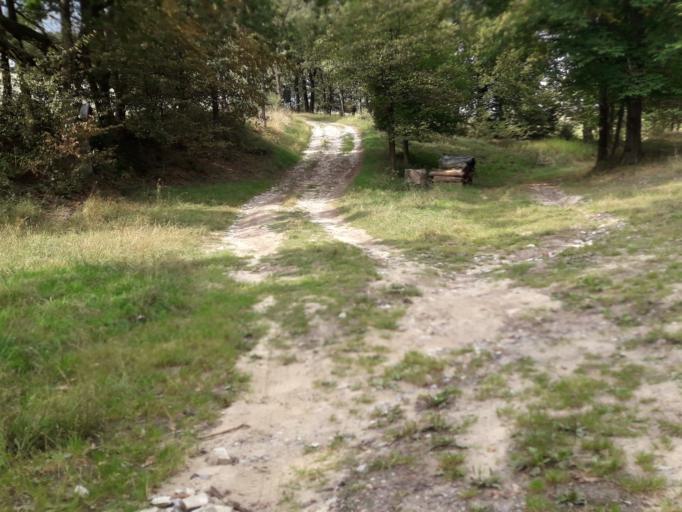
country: DE
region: North Rhine-Westphalia
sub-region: Regierungsbezirk Detmold
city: Schlangen
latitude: 51.8320
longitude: 8.8715
